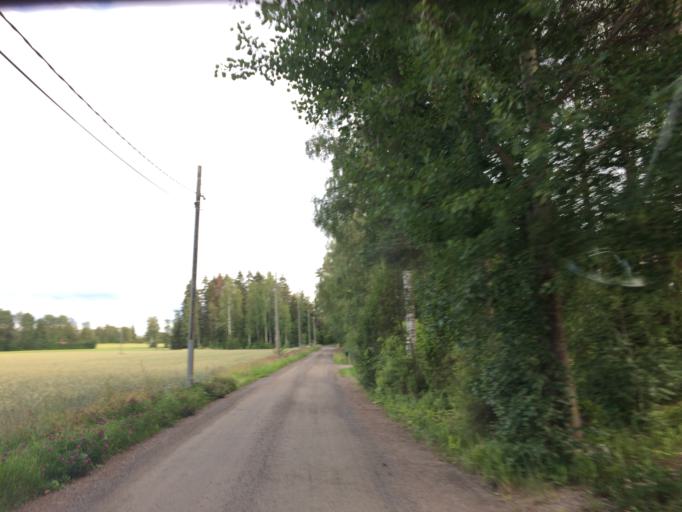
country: FI
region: Haeme
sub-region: Haemeenlinna
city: Tervakoski
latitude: 60.8540
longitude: 24.6240
